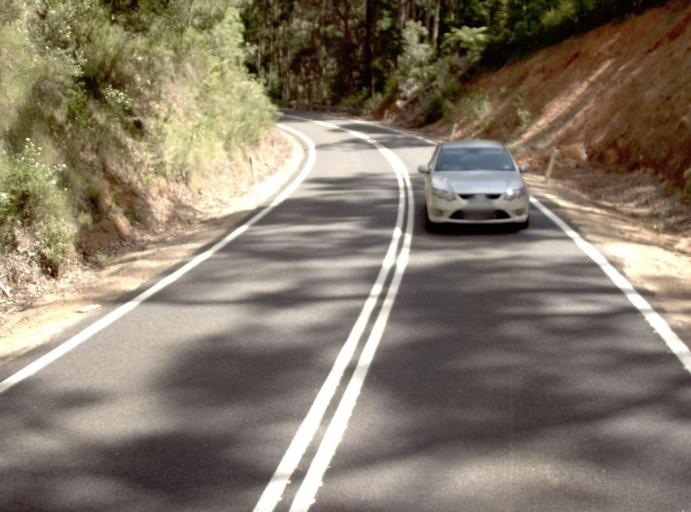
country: AU
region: New South Wales
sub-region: Bombala
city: Bombala
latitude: -37.5503
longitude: 149.3591
